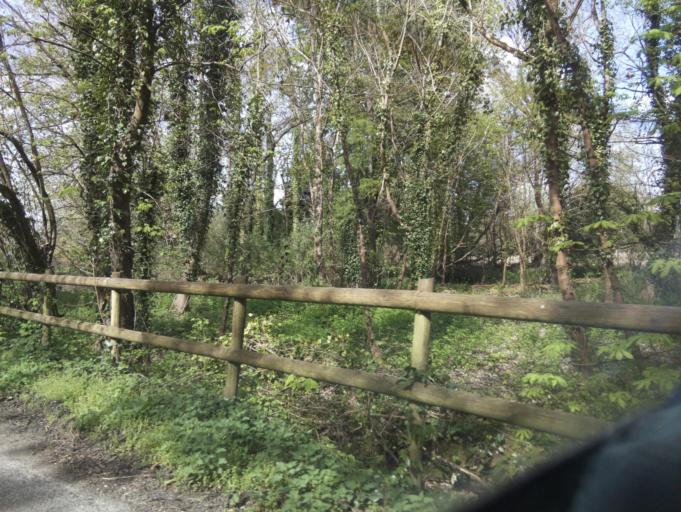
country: GB
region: England
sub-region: Hampshire
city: Romsey
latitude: 51.0793
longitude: -1.5163
